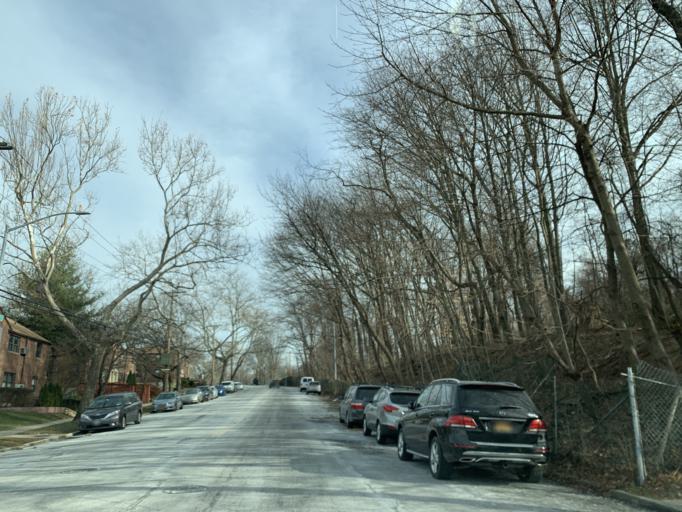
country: US
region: New York
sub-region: Nassau County
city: Lake Success
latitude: 40.7557
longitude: -73.7369
